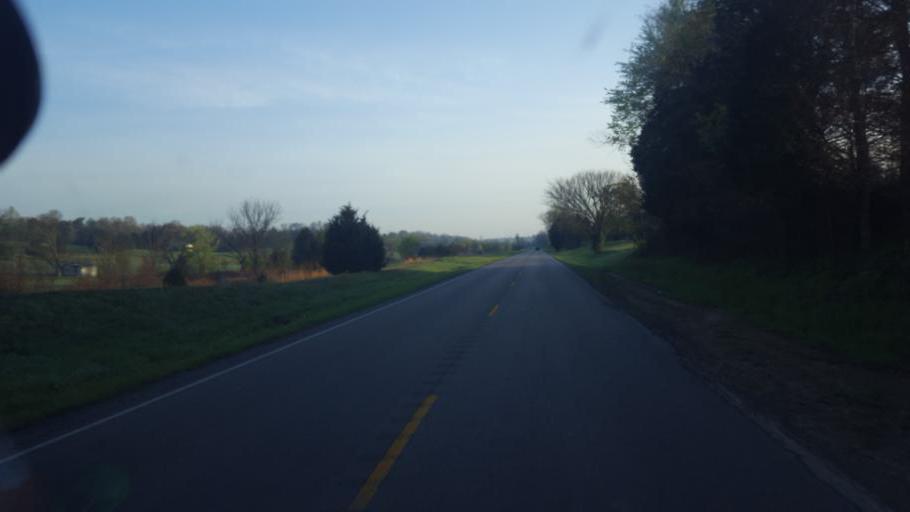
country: US
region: Kentucky
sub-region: Hart County
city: Munfordville
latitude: 37.3557
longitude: -85.9079
